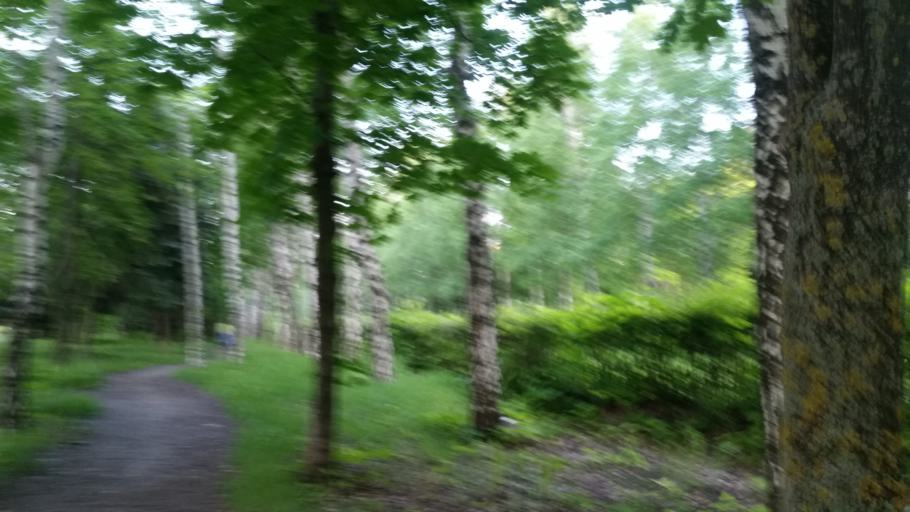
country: RU
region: Ulyanovsk
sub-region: Ulyanovskiy Rayon
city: Ulyanovsk
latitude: 54.3471
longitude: 48.3948
